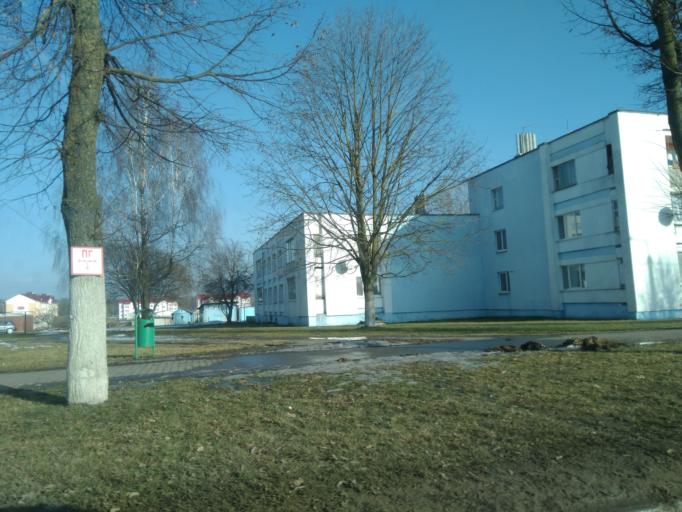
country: BY
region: Minsk
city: Snow
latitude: 53.2188
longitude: 26.4028
